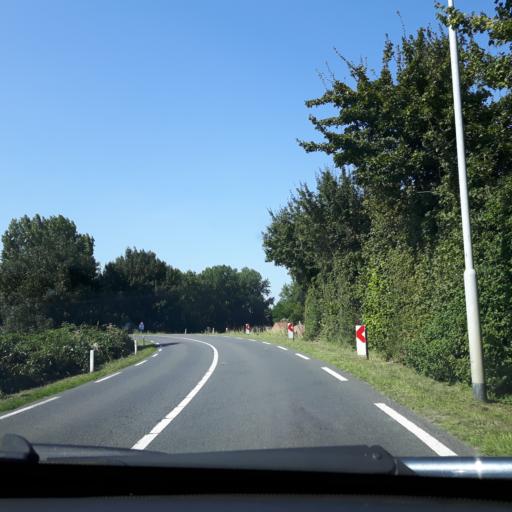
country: NL
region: Zeeland
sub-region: Gemeente Reimerswaal
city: Yerseke
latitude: 51.4847
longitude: 4.0498
